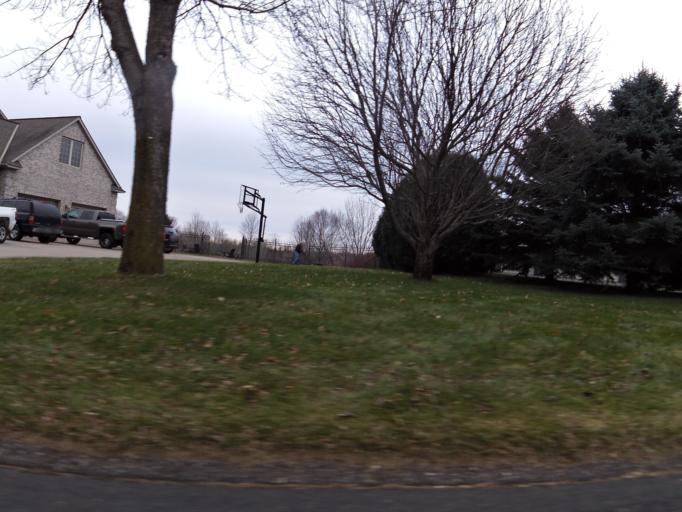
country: US
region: Minnesota
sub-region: Washington County
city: Lake Elmo
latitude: 44.9889
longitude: -92.8706
